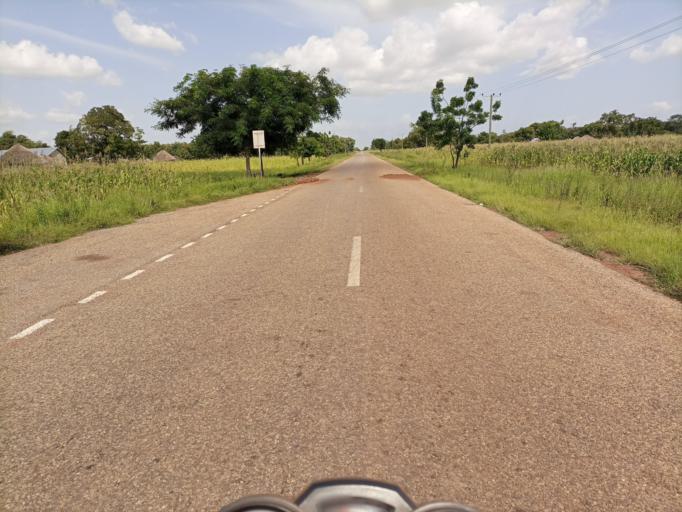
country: GH
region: Northern
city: Savelugu
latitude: 9.5735
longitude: -1.0077
